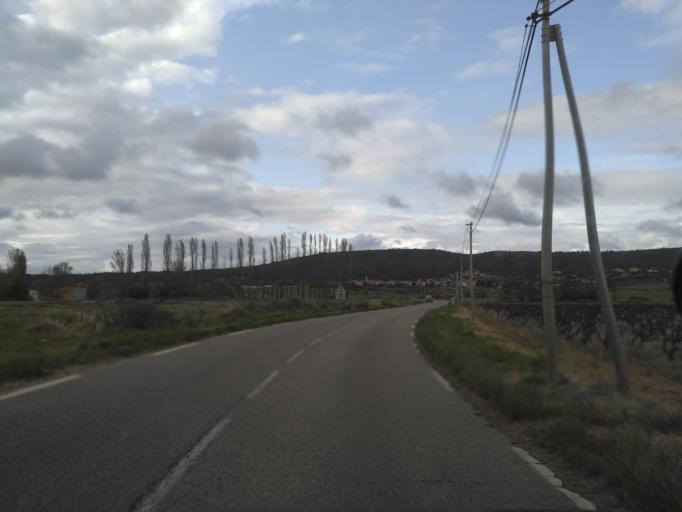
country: FR
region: Provence-Alpes-Cote d'Azur
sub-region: Departement du Var
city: Barjols
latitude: 43.5802
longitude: 6.0151
